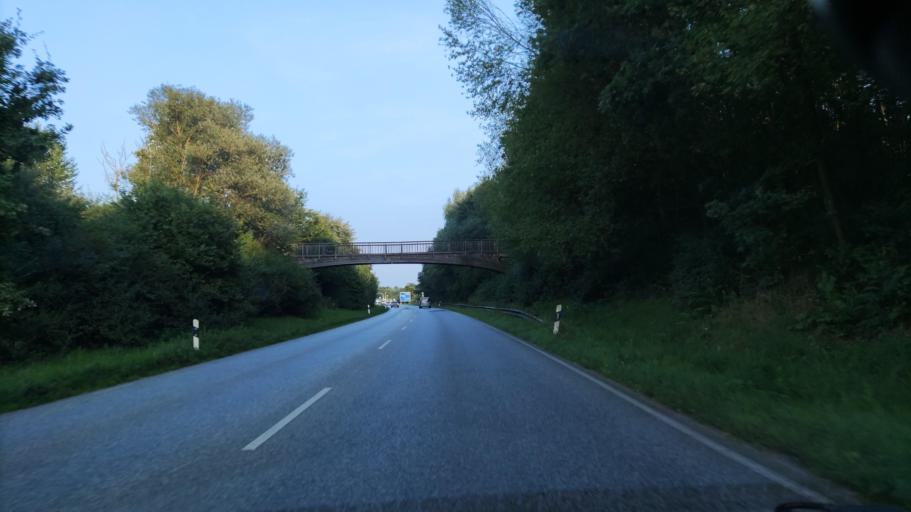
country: DE
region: Schleswig-Holstein
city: Braak
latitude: 53.6433
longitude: 10.2642
